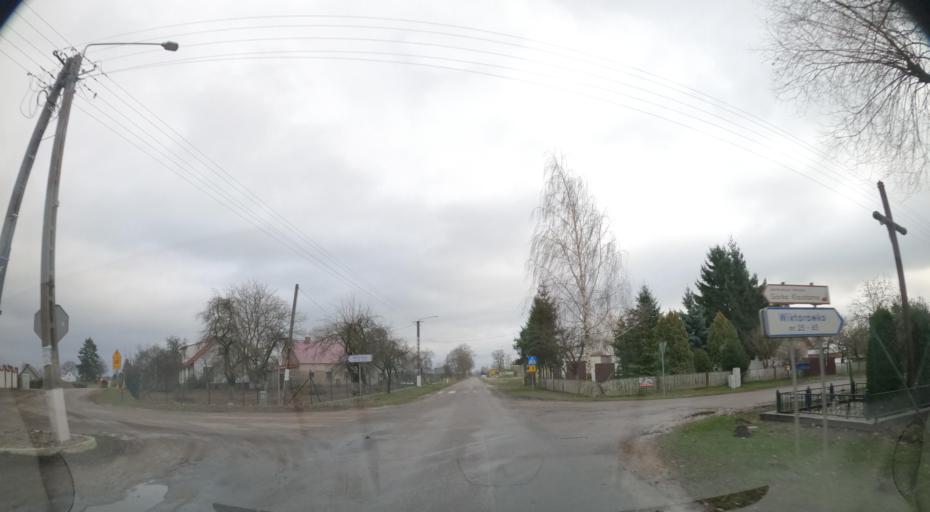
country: PL
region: Greater Poland Voivodeship
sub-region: Powiat pilski
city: Lobzenica
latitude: 53.2681
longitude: 17.2000
